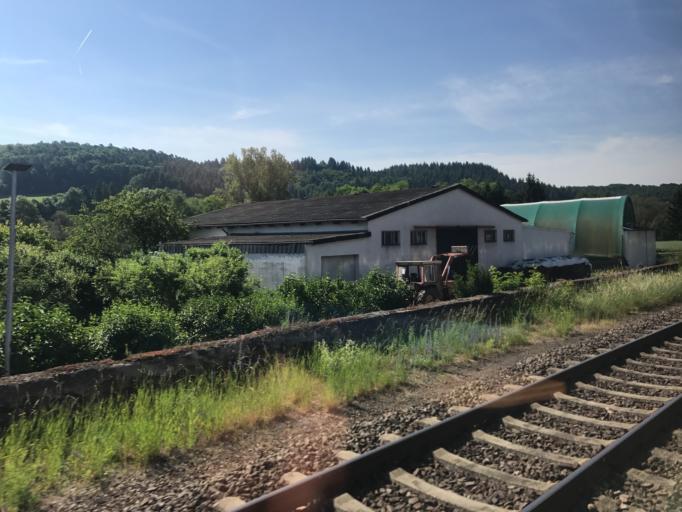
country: DE
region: Rheinland-Pfalz
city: Barenbach
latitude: 49.7616
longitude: 7.4349
